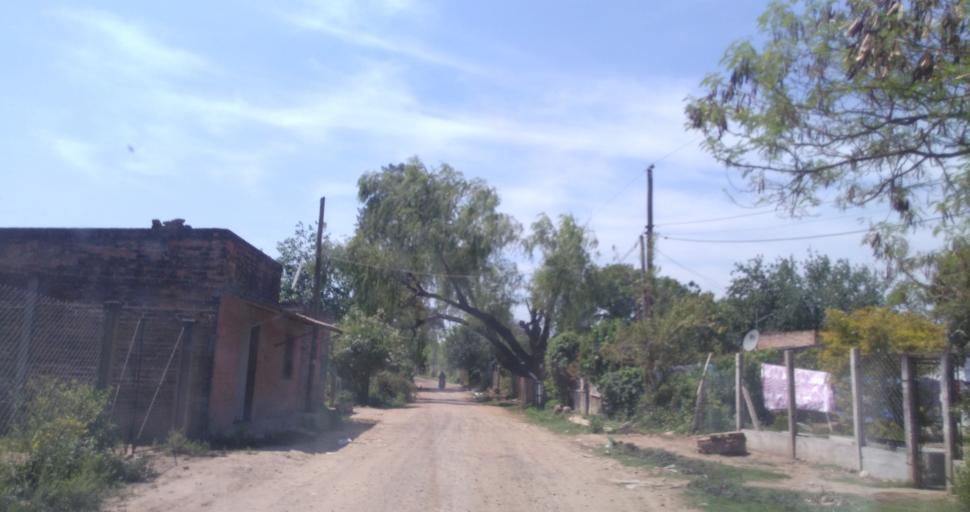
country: AR
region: Chaco
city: Fontana
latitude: -27.4222
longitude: -59.0136
